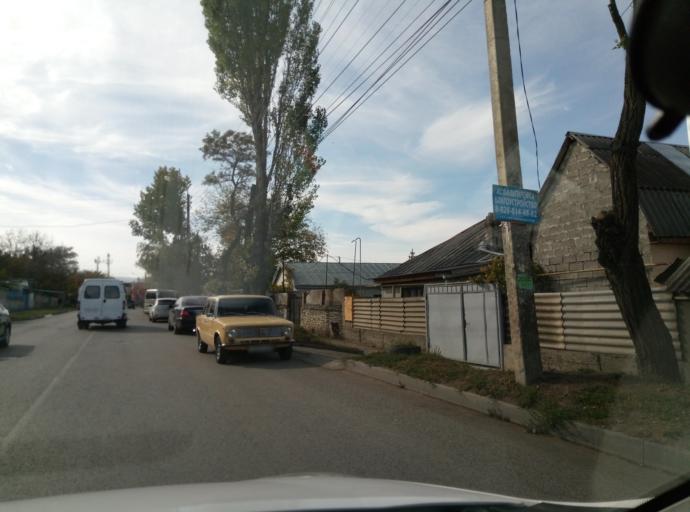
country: RU
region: Stavropol'skiy
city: Kislovodsk
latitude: 43.9265
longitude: 42.7094
